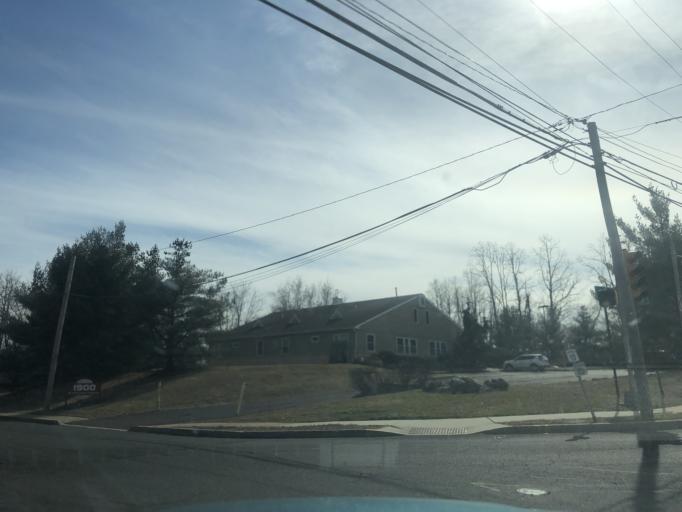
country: US
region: Pennsylvania
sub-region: Bucks County
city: Langhorne
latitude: 40.1576
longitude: -74.9440
